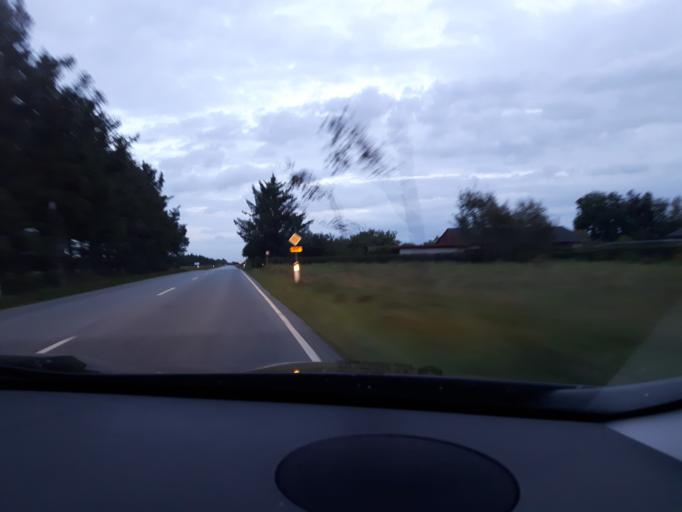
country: DK
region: North Denmark
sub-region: Hjorring Kommune
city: Hirtshals
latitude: 57.5239
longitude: 9.9499
